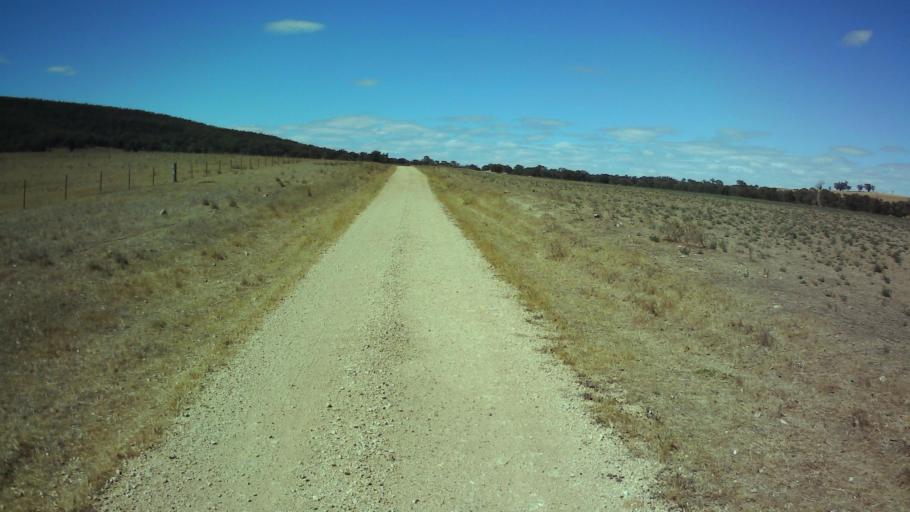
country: AU
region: New South Wales
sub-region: Weddin
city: Grenfell
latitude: -34.0358
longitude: 148.4339
